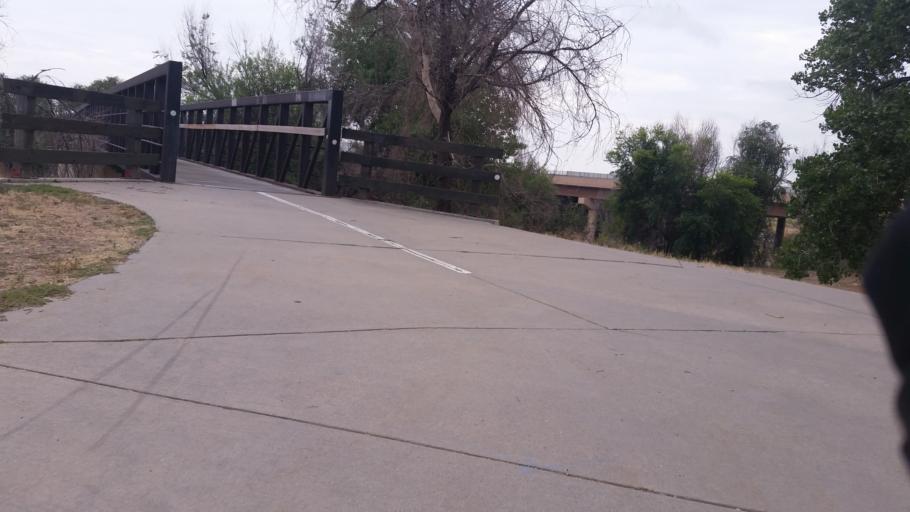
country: US
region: Colorado
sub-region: Adams County
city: Welby
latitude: 39.8271
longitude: -104.9498
